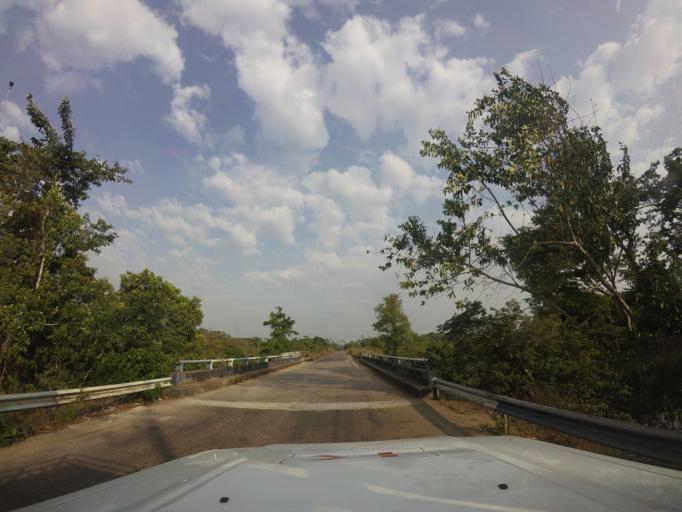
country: LR
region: Grand Cape Mount
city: Robertsport
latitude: 6.8607
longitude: -11.1910
